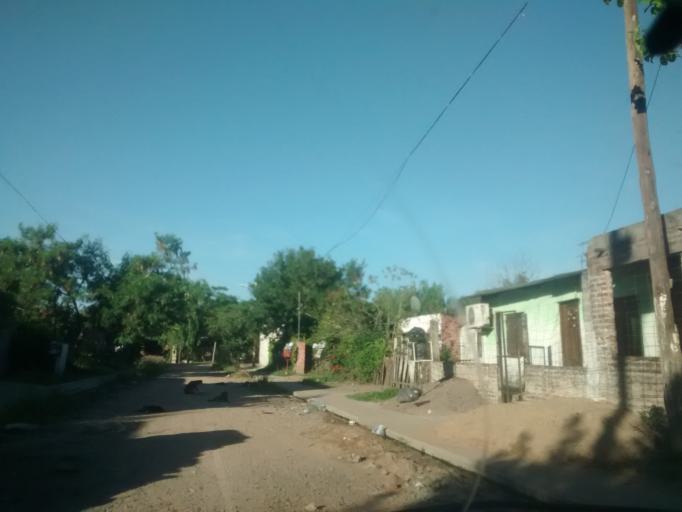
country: AR
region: Chaco
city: Fontana
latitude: -27.4563
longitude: -59.0283
